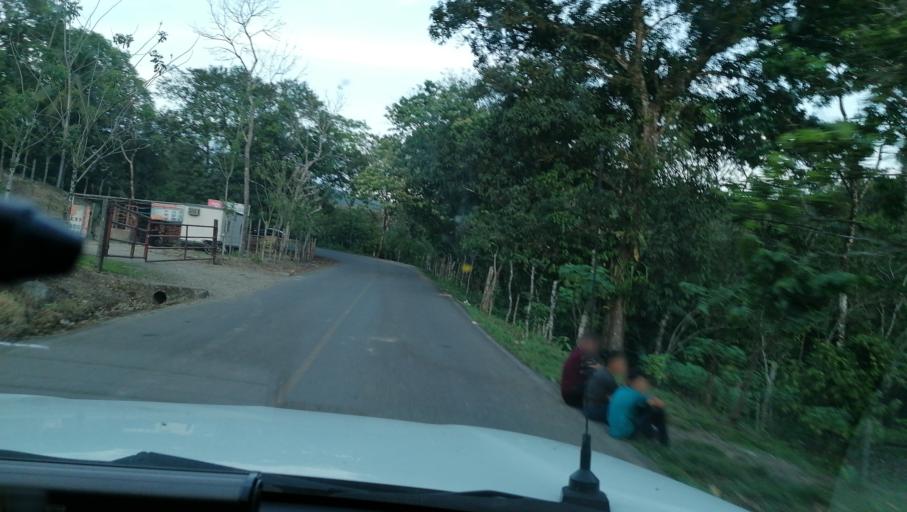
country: MX
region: Chiapas
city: Ostuacan
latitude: 17.4192
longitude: -93.3393
